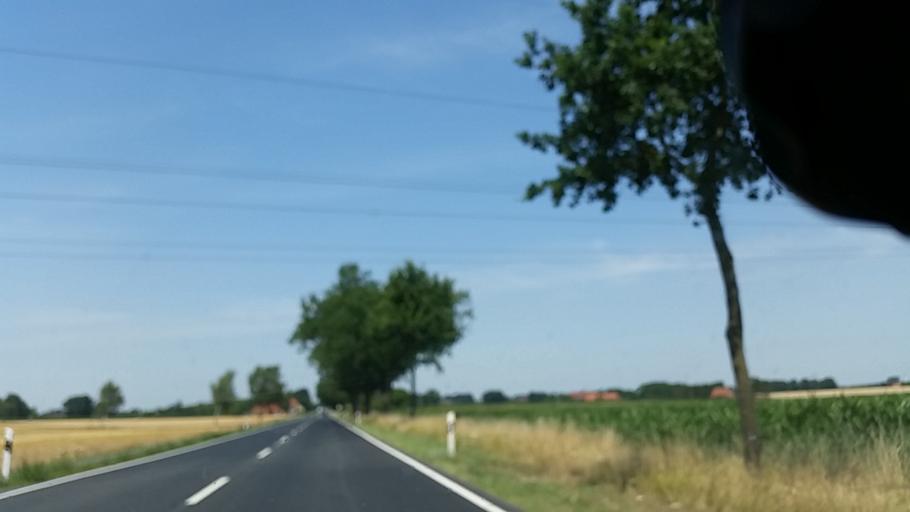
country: DE
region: Lower Saxony
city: Asendorf
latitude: 52.7449
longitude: 9.0221
